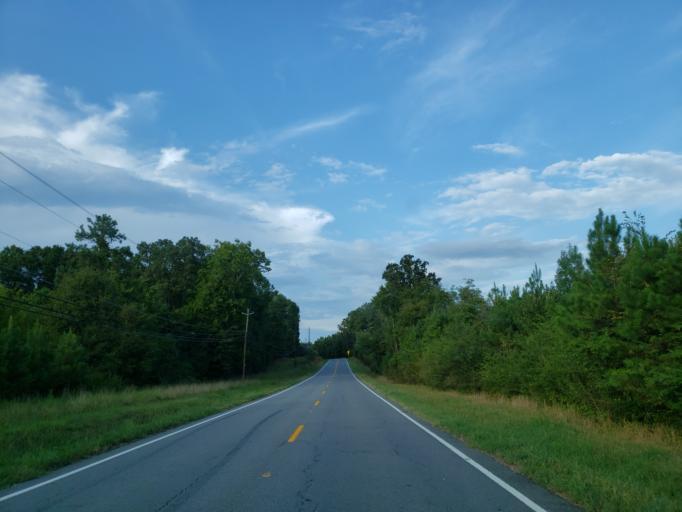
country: US
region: Georgia
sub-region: Bartow County
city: Euharlee
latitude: 34.2417
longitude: -84.9216
